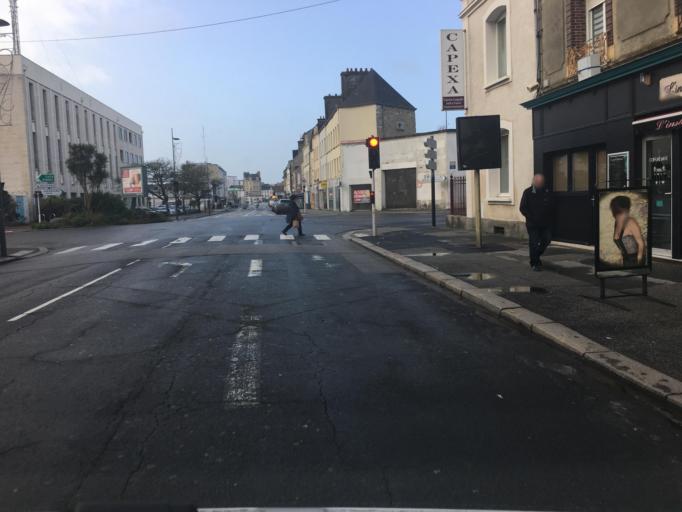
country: FR
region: Lower Normandy
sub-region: Departement de la Manche
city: Cherbourg-Octeville
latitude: 49.6389
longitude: -1.6159
